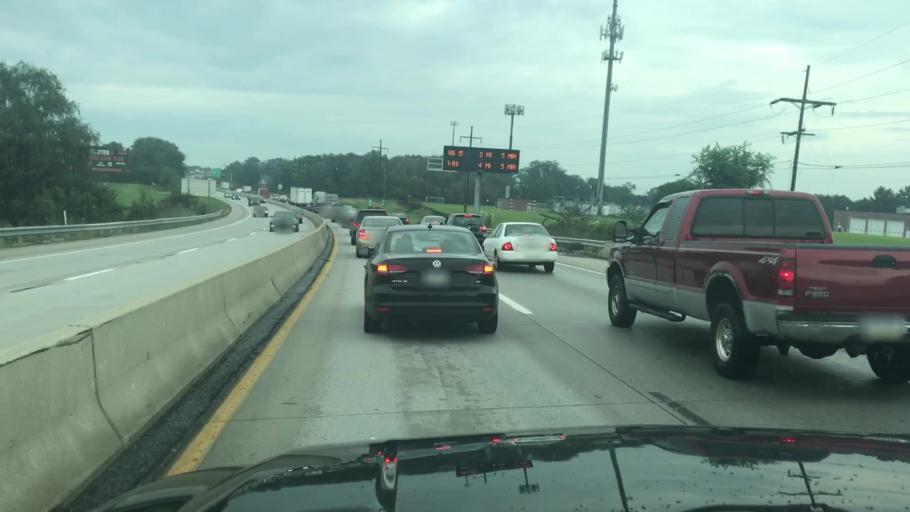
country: US
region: Pennsylvania
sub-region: Cumberland County
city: Shiremanstown
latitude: 40.2345
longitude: -76.9702
